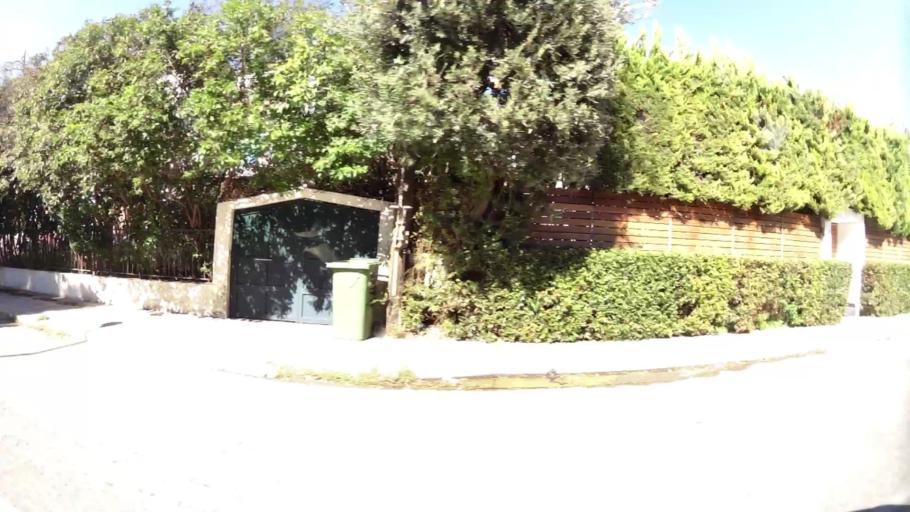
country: GR
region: Attica
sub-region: Nomarchia Athinas
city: Nea Erythraia
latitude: 38.0948
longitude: 23.8067
